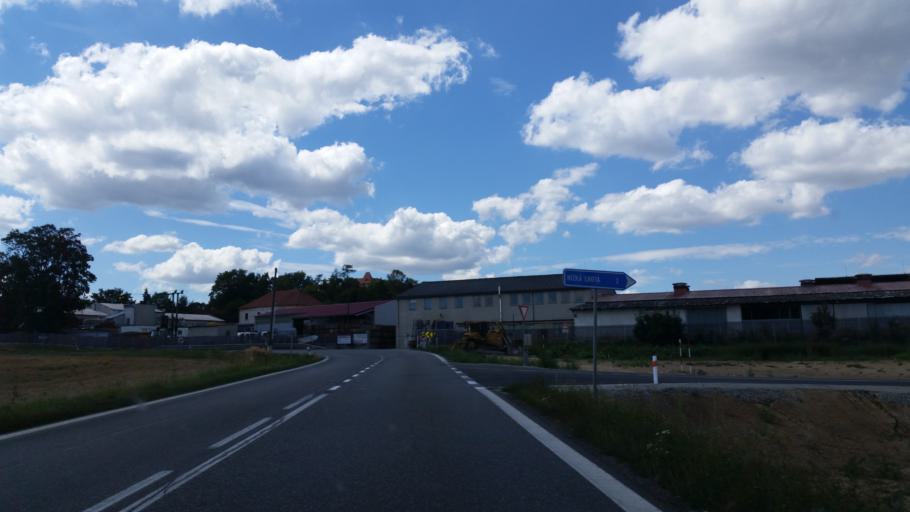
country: CZ
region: Vysocina
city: Pacov
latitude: 49.4249
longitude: 15.0197
